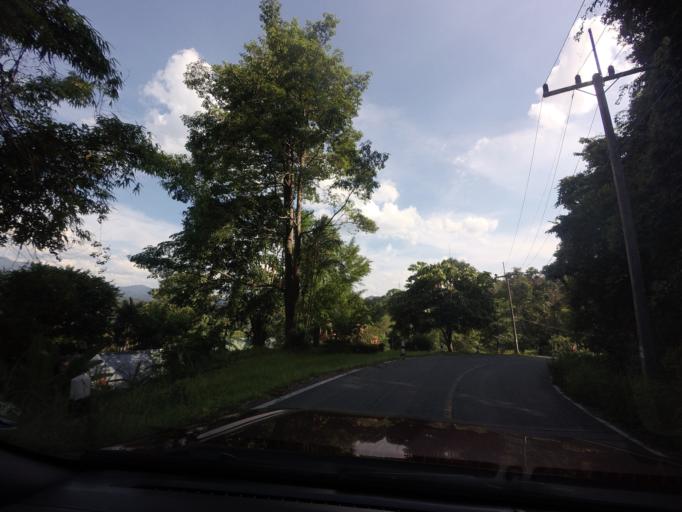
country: TH
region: Yala
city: Than To
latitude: 6.0671
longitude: 101.3666
